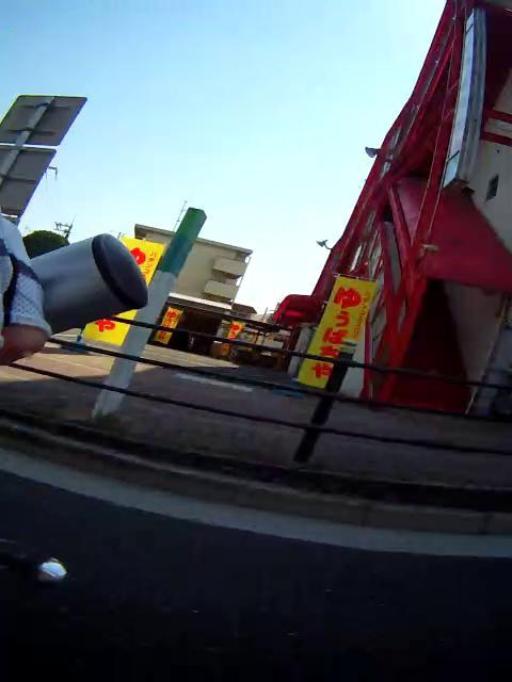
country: JP
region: Osaka
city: Yao
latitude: 34.6445
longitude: 135.5536
